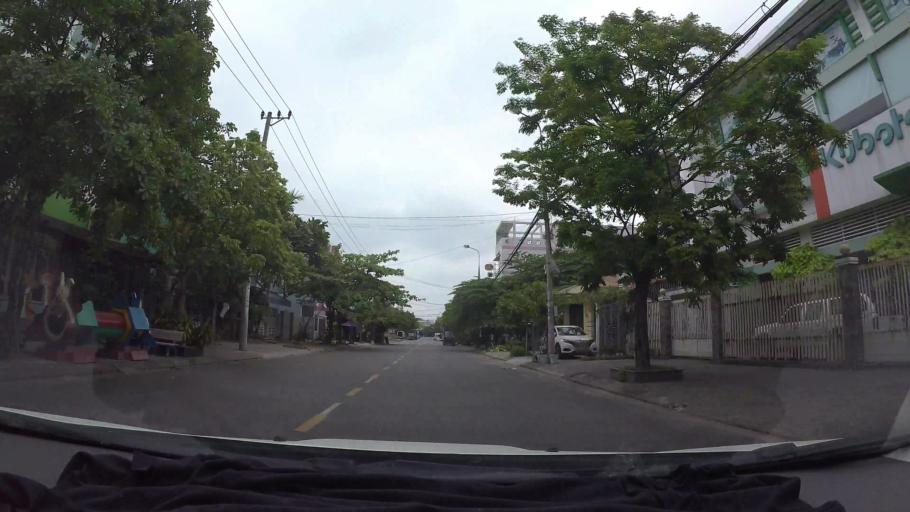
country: VN
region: Da Nang
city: Lien Chieu
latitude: 16.0603
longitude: 108.1736
